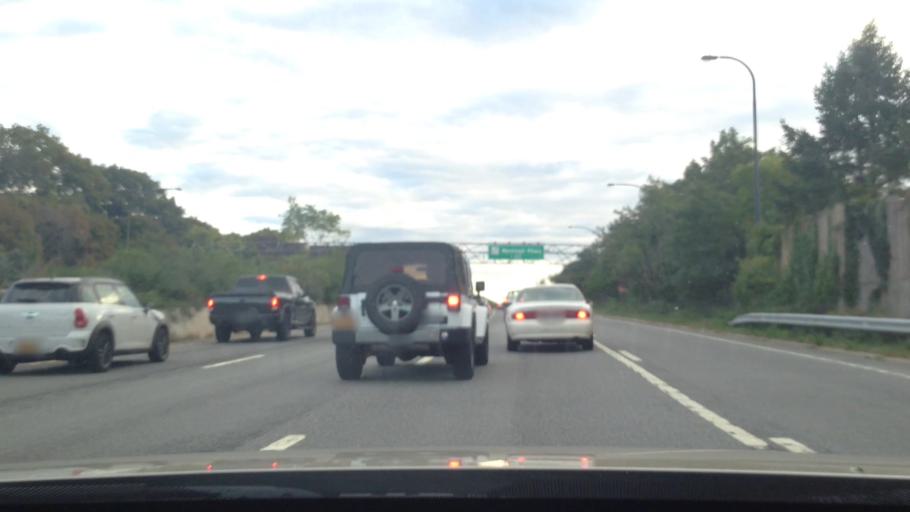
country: US
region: New York
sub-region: Nassau County
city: Westbury
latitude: 40.7641
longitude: -73.5845
